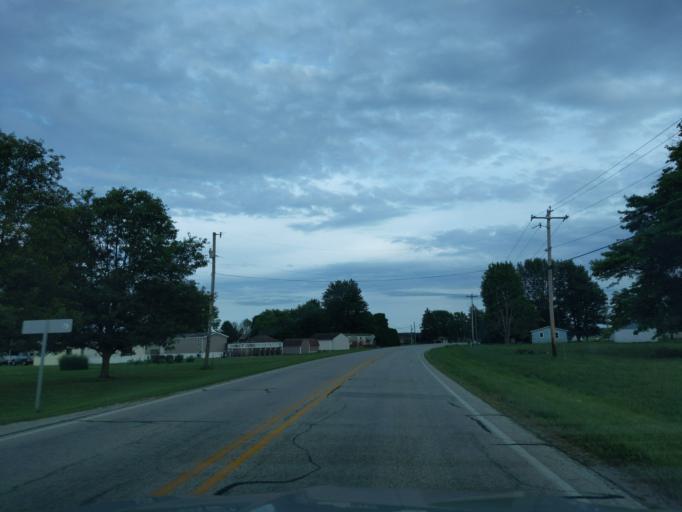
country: US
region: Indiana
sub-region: Ripley County
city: Sunman
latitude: 39.2676
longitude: -85.0959
